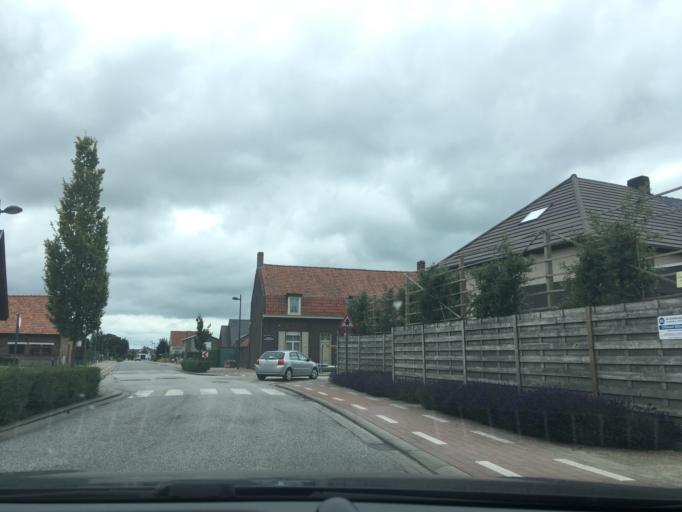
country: BE
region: Flanders
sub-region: Provincie West-Vlaanderen
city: Wingene
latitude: 51.0616
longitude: 3.2825
